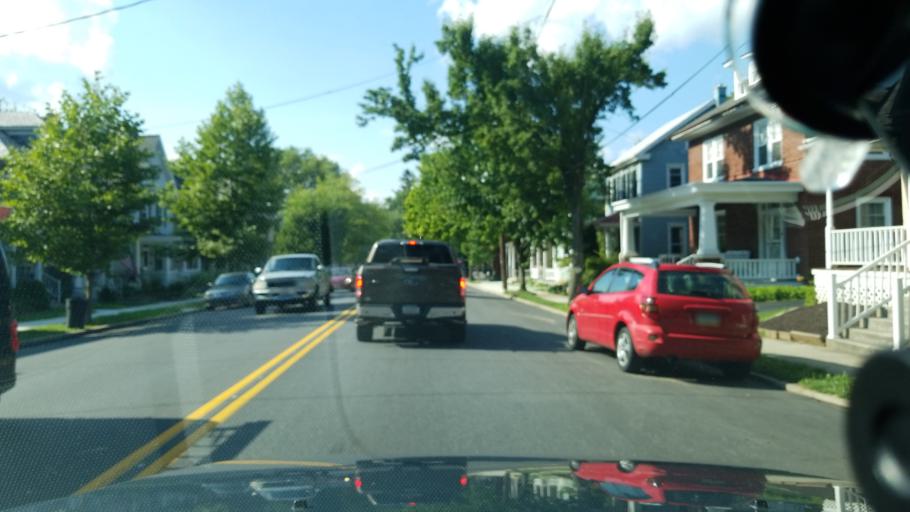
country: US
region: Pennsylvania
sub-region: Lancaster County
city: Lititz
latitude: 40.1508
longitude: -76.3070
